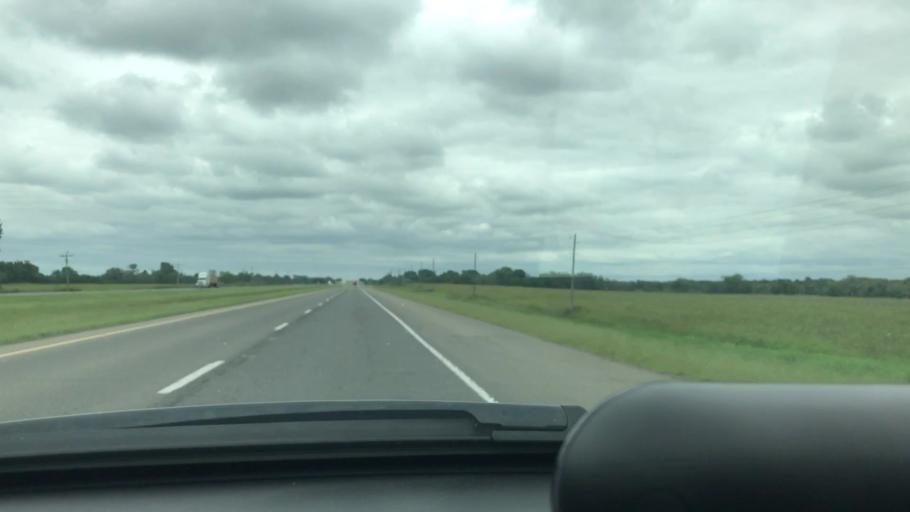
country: US
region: Oklahoma
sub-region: Wagoner County
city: Wagoner
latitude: 35.8589
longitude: -95.4025
